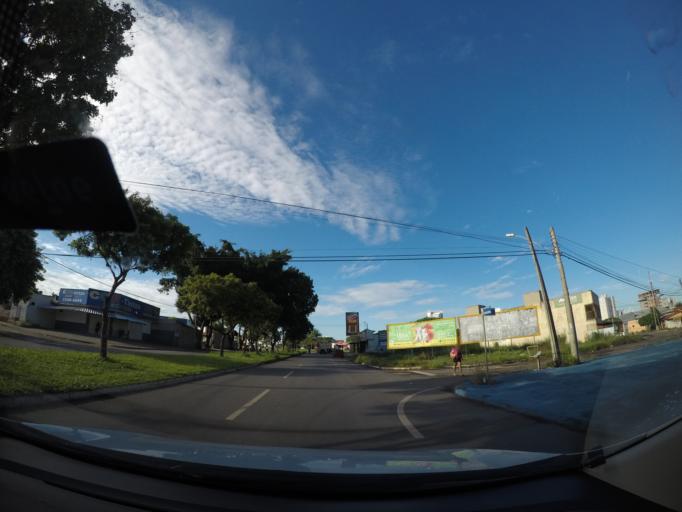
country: BR
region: Goias
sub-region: Goiania
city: Goiania
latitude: -16.7368
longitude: -49.2730
